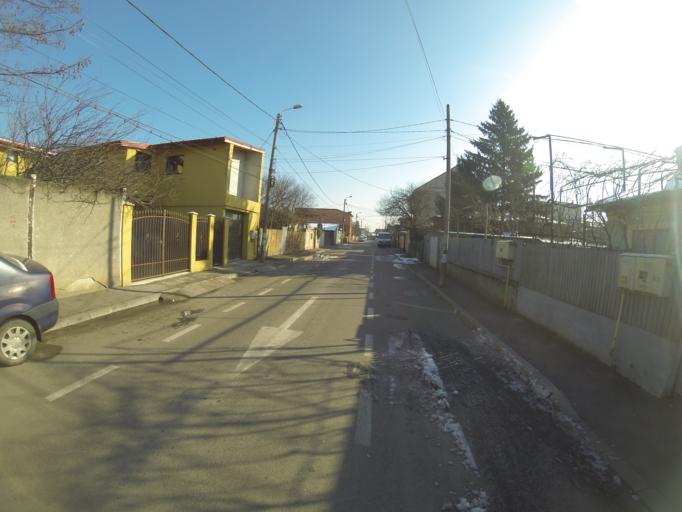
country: RO
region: Bucuresti
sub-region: Municipiul Bucuresti
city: Bucuresti
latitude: 44.3977
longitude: 26.0626
